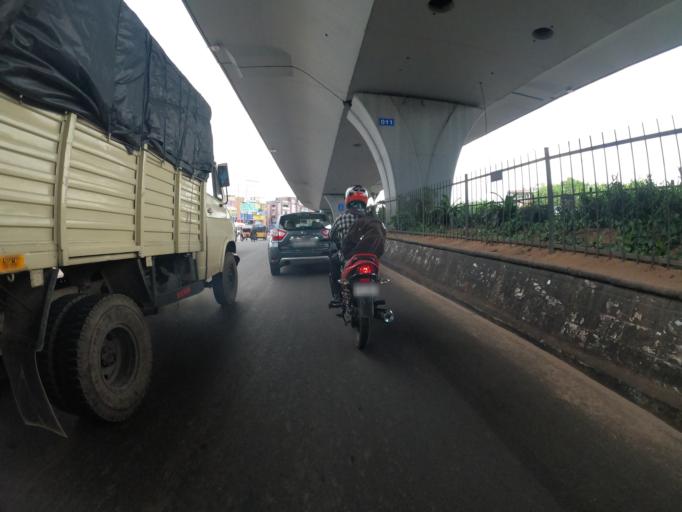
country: IN
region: Telangana
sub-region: Hyderabad
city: Hyderabad
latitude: 17.3953
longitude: 78.4404
